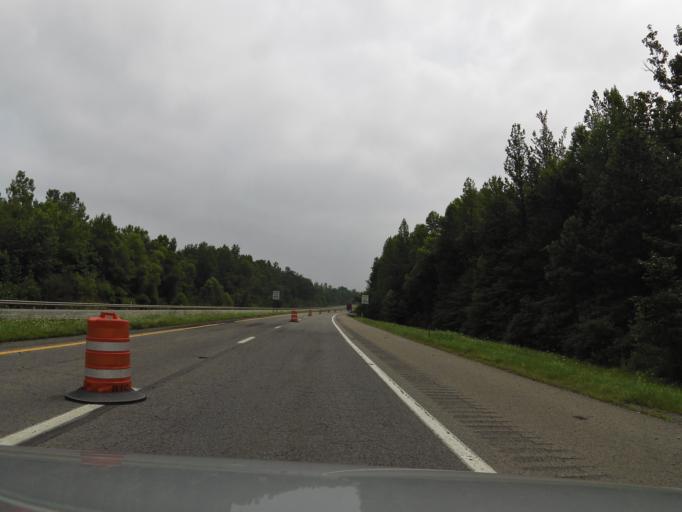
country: US
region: Kentucky
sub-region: Muhlenberg County
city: Morehead
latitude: 37.2710
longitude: -87.1580
